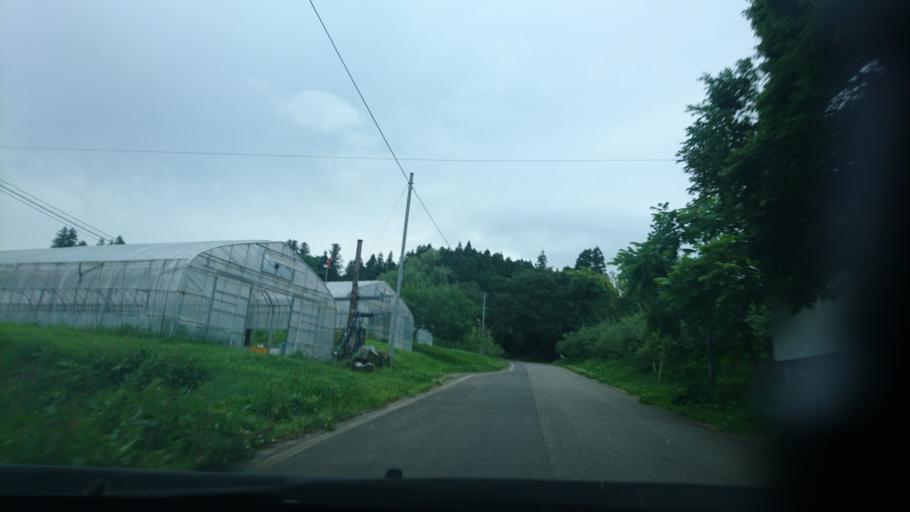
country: JP
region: Iwate
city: Ichinoseki
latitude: 38.8962
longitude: 141.3095
